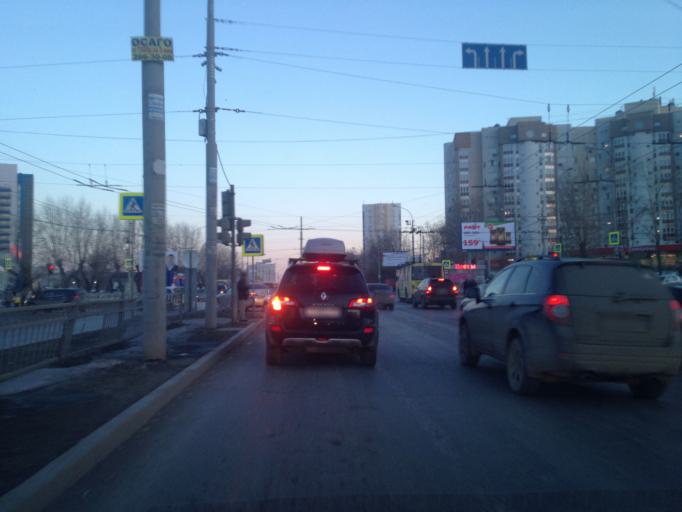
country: RU
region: Sverdlovsk
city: Yekaterinburg
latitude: 56.7927
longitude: 60.6427
